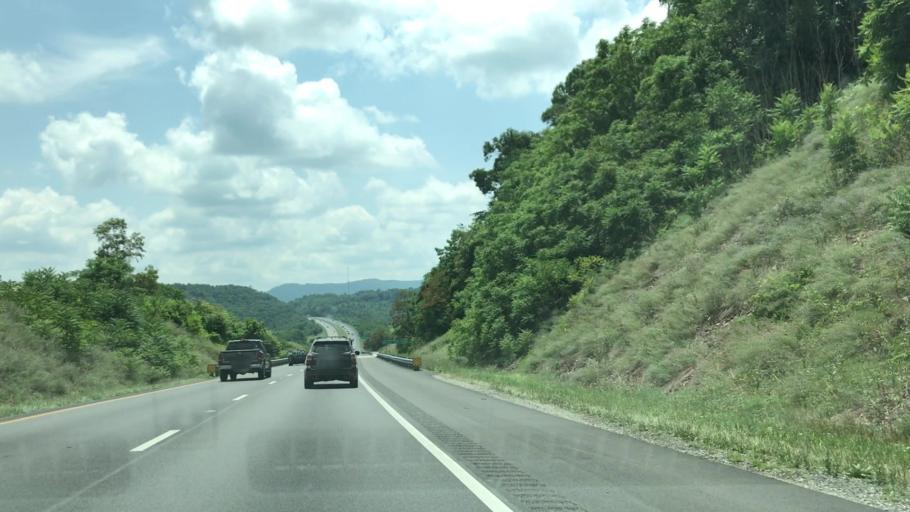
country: US
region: Virginia
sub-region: Pulaski County
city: Pulaski
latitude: 36.8991
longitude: -80.8758
